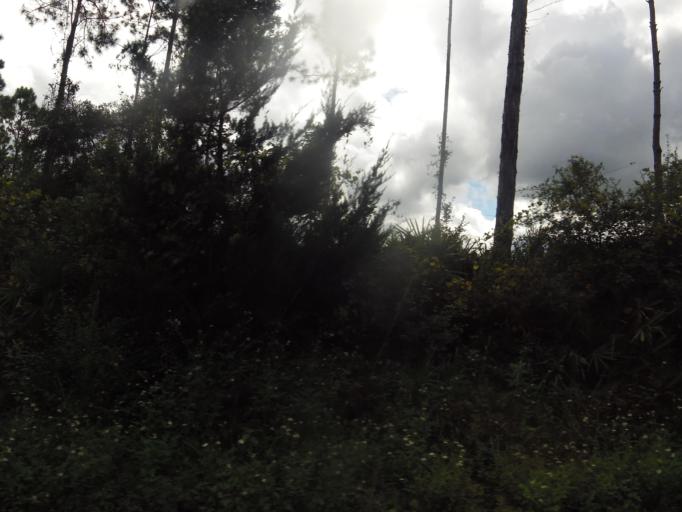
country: US
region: Florida
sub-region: Saint Johns County
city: Palm Valley
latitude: 30.0525
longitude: -81.3906
